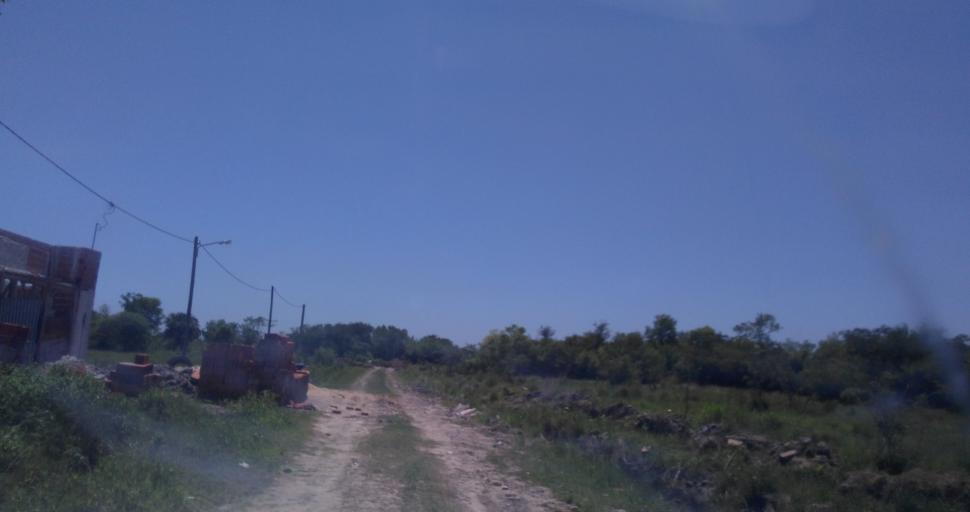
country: AR
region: Chaco
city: Fontana
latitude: -27.4036
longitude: -58.9702
